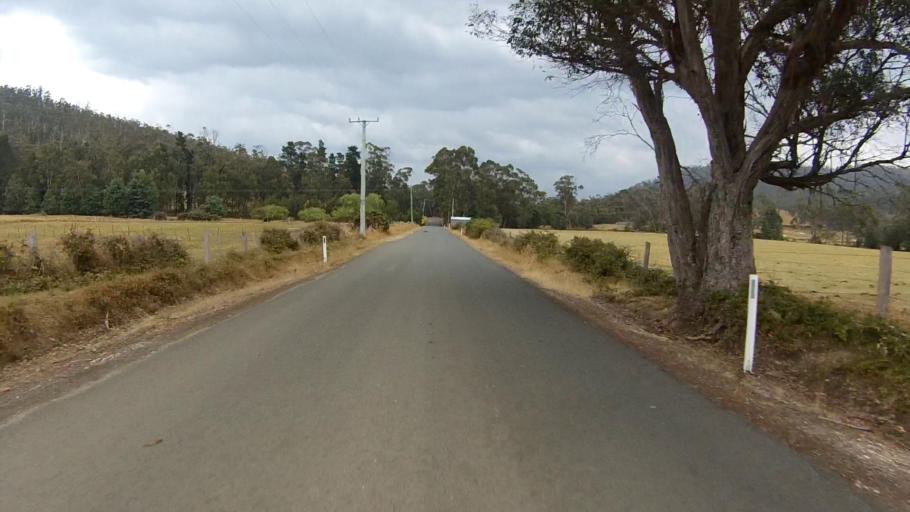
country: AU
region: Tasmania
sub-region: Huon Valley
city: Cygnet
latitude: -43.2383
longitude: 147.1544
